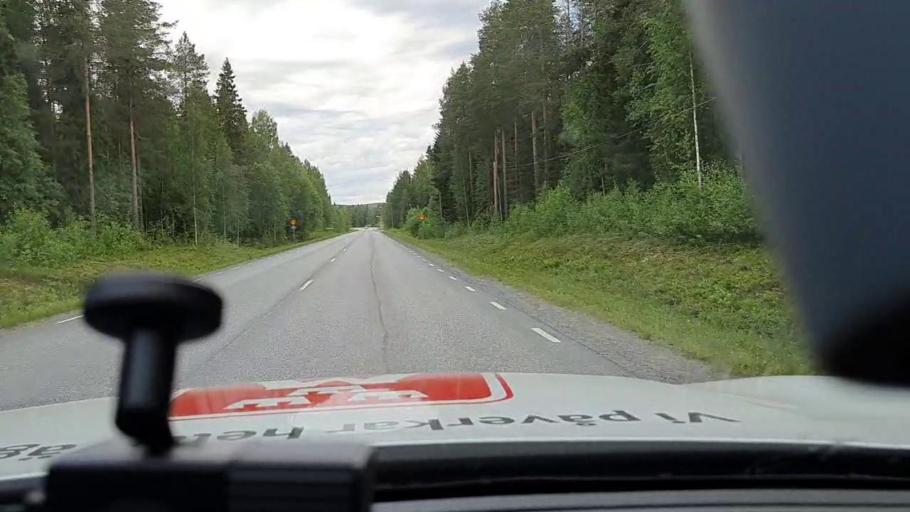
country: SE
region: Norrbotten
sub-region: Bodens Kommun
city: Boden
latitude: 65.8098
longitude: 21.6530
